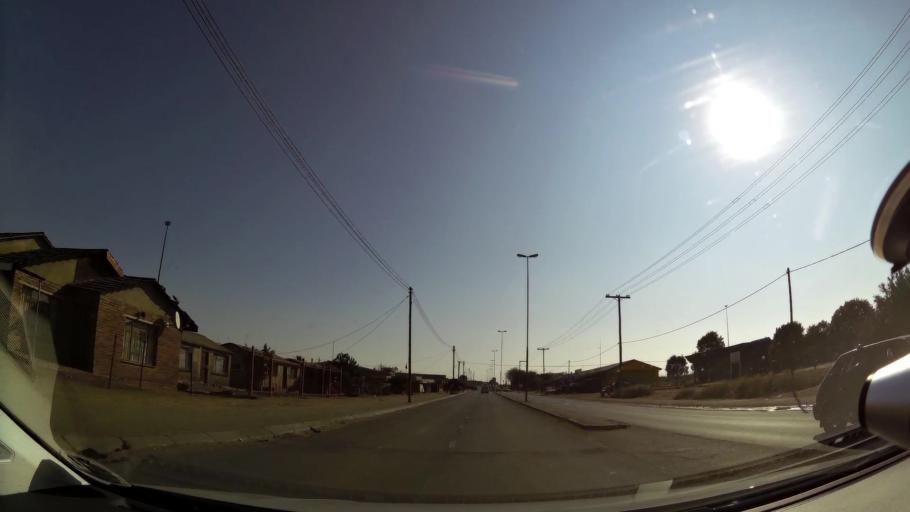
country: ZA
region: Orange Free State
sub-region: Mangaung Metropolitan Municipality
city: Bloemfontein
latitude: -29.1863
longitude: 26.2346
